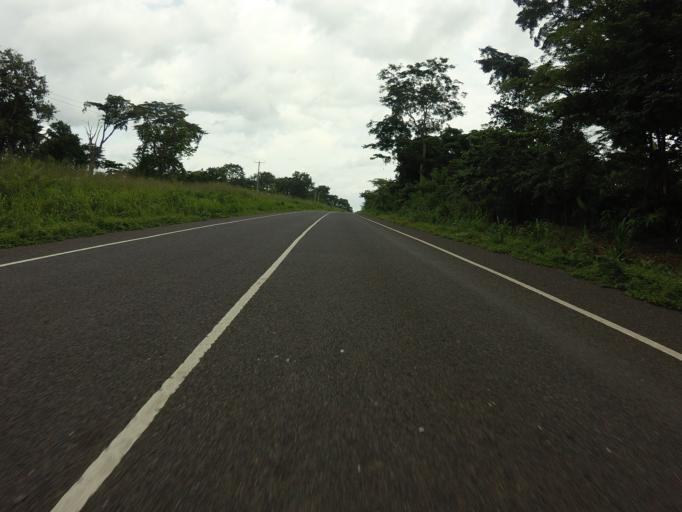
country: TG
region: Plateaux
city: Badou
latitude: 7.9810
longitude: 0.5606
